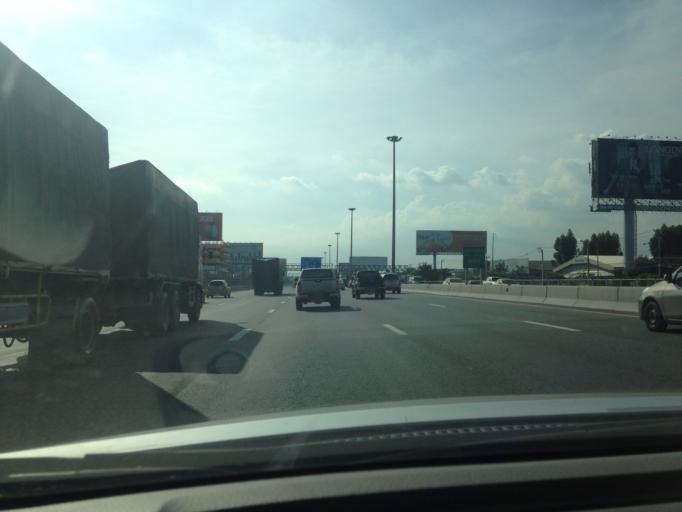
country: TH
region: Bangkok
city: Saphan Sung
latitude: 13.7304
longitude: 100.7220
